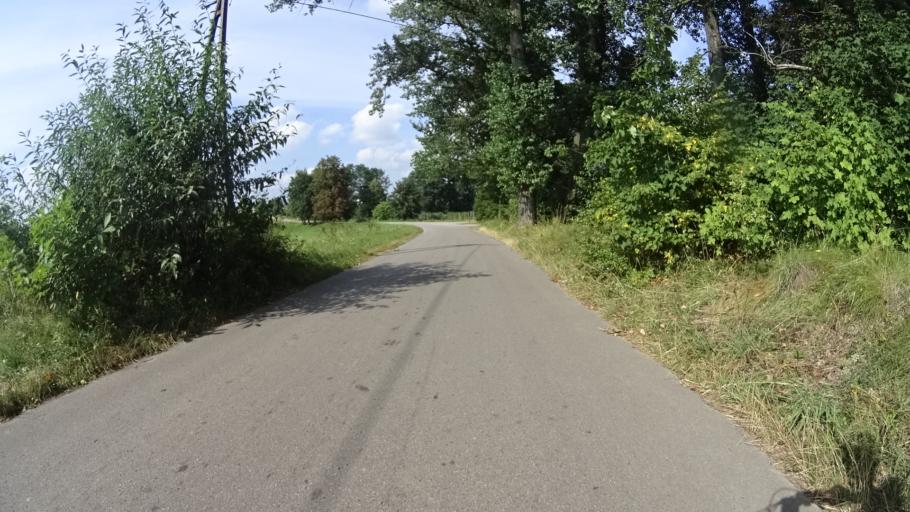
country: PL
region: Masovian Voivodeship
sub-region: Powiat grojecki
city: Goszczyn
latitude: 51.6987
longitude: 20.8480
